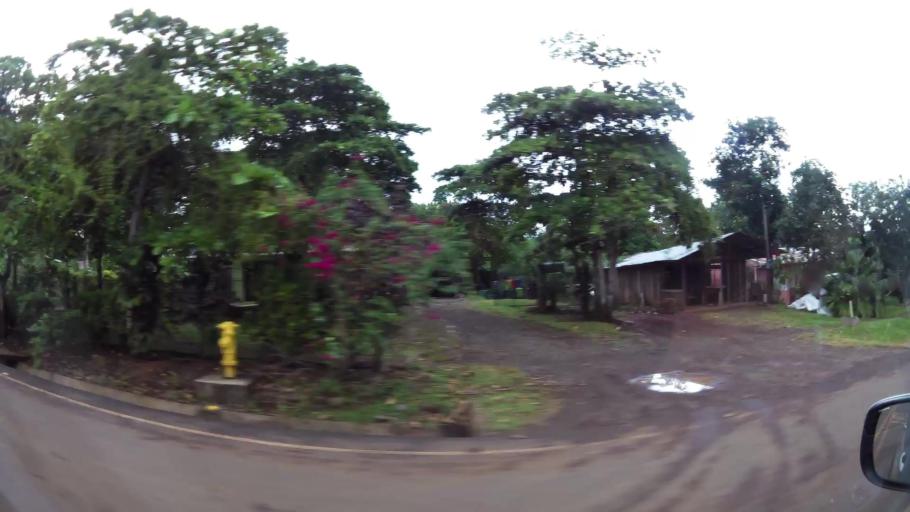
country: CR
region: Puntarenas
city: Esparza
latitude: 9.9597
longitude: -84.5916
